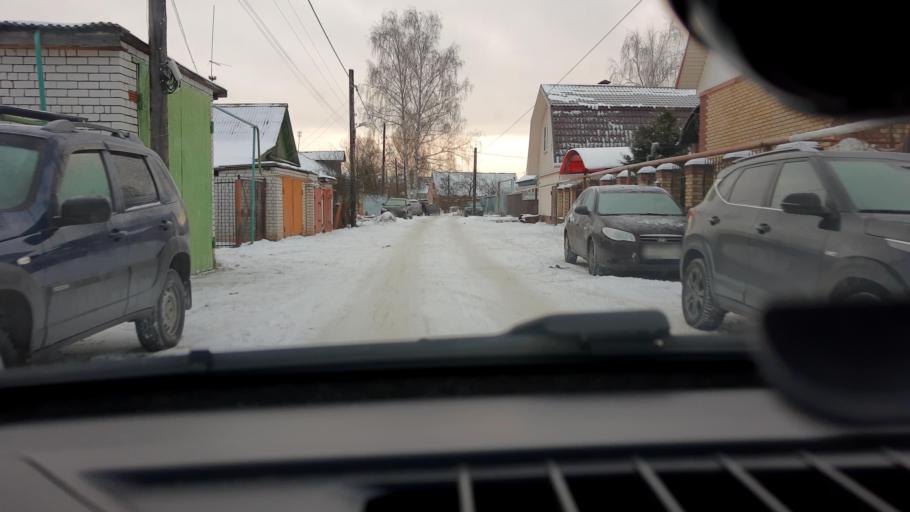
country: RU
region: Nizjnij Novgorod
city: Gorbatovka
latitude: 56.3732
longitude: 43.8270
